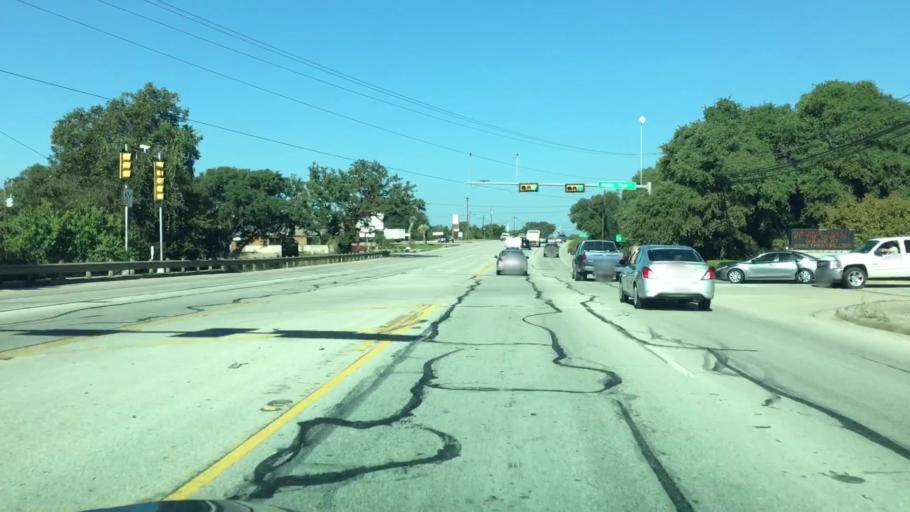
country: US
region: Texas
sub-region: Hays County
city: Dripping Springs
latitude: 30.1944
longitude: -98.1017
